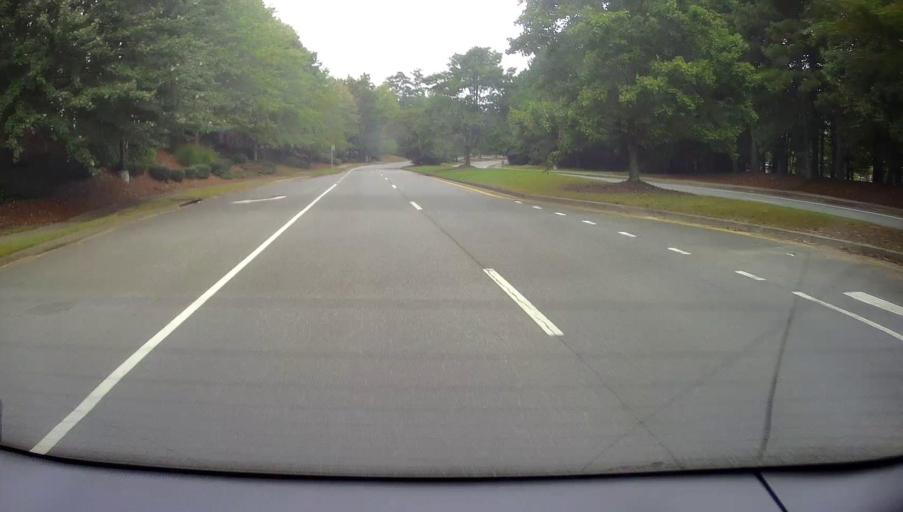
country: US
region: Georgia
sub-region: Fulton County
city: Alpharetta
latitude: 34.1005
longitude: -84.2650
